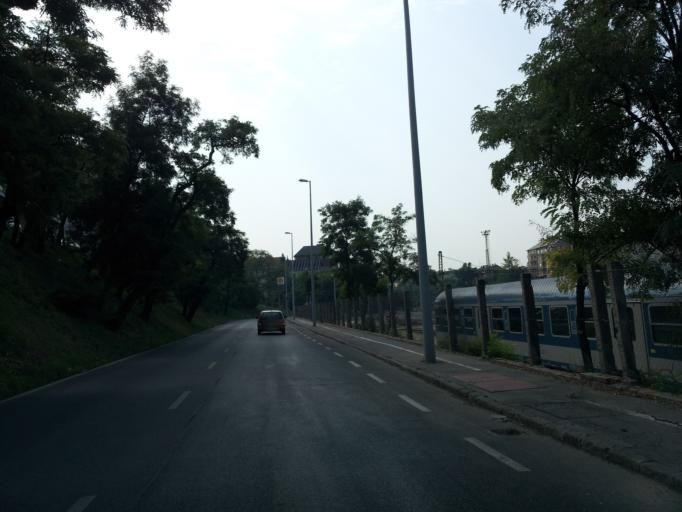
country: HU
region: Budapest
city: Budapest I. keruelet
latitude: 47.4930
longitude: 19.0298
